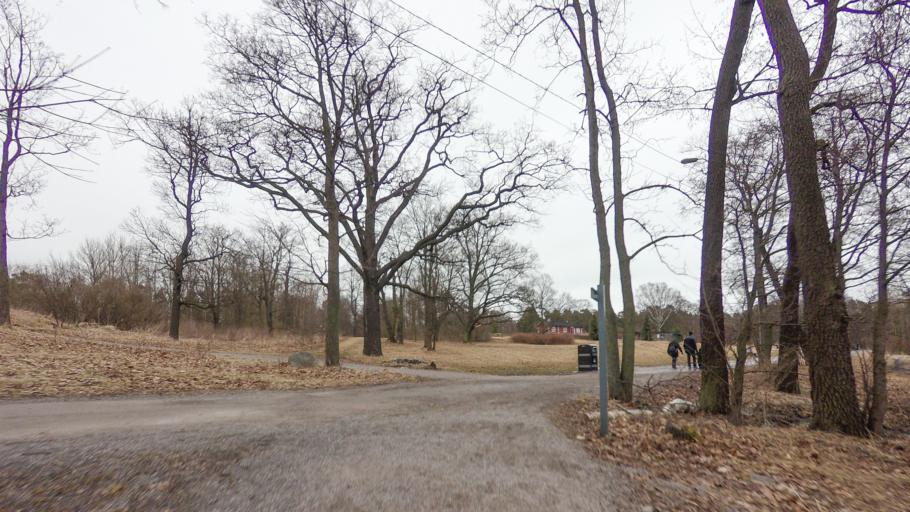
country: FI
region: Uusimaa
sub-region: Helsinki
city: Helsinki
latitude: 60.1795
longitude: 24.9838
